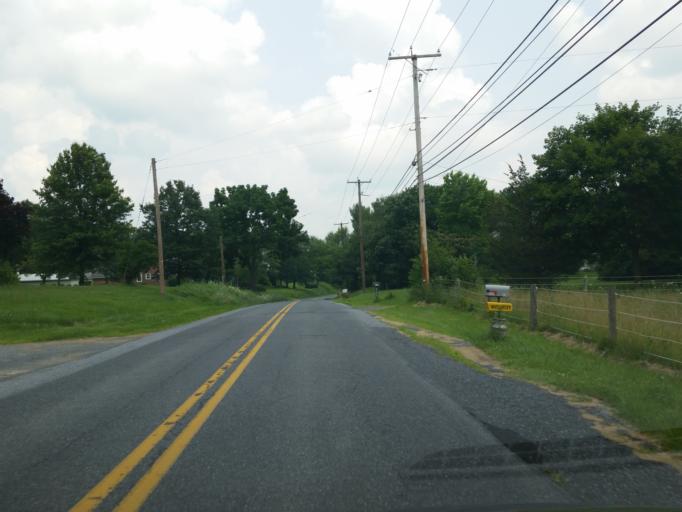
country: US
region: Pennsylvania
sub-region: Lebanon County
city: Palmyra
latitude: 40.3854
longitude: -76.6351
